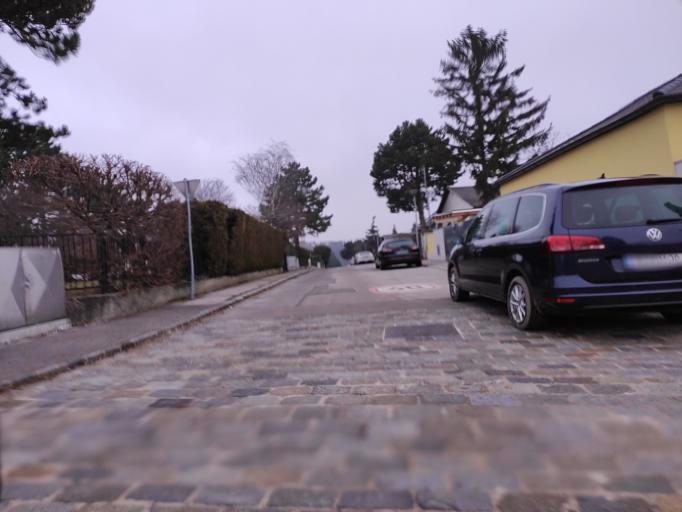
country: AT
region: Lower Austria
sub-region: Politischer Bezirk Modling
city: Hinterbruehl
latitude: 48.0961
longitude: 16.2607
